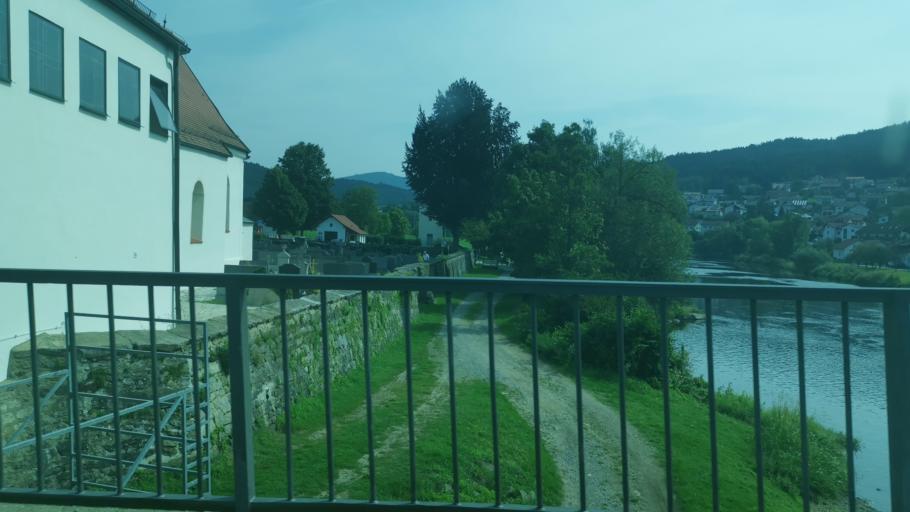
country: DE
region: Bavaria
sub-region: Upper Palatinate
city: Chamerau
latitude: 49.1985
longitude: 12.7457
